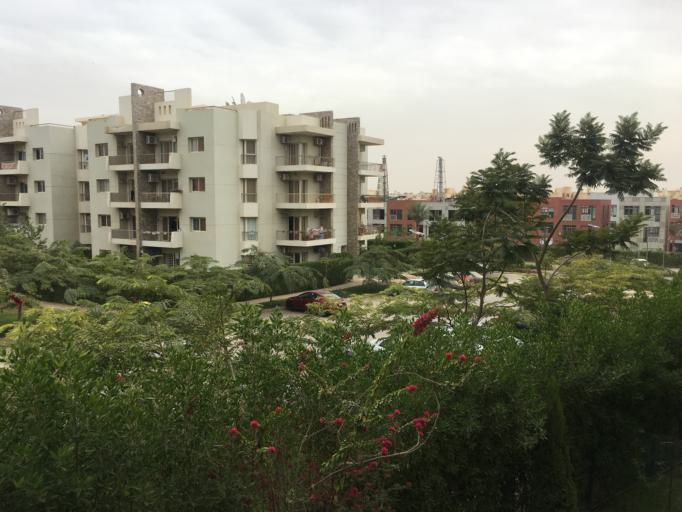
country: EG
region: Al Jizah
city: Awsim
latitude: 30.0437
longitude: 30.9802
